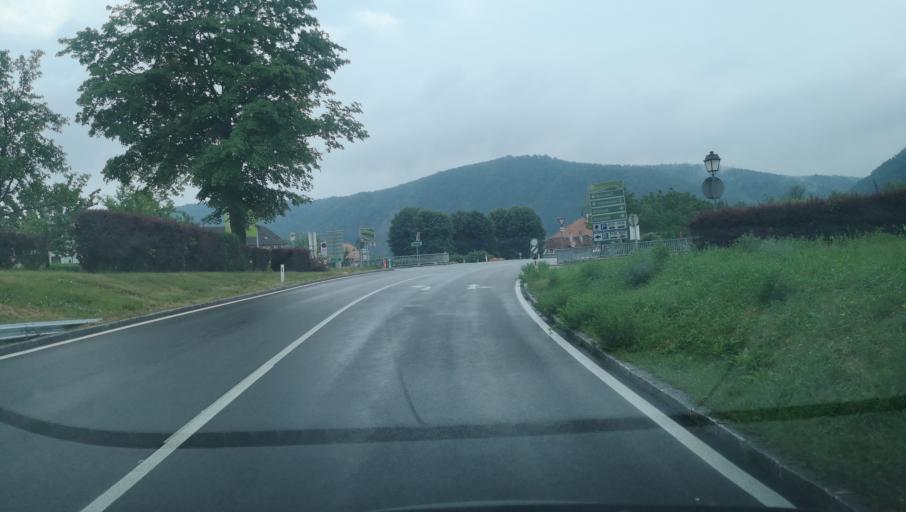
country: AT
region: Lower Austria
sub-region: Politischer Bezirk Krems
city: Durnstein
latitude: 48.3936
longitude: 15.5233
